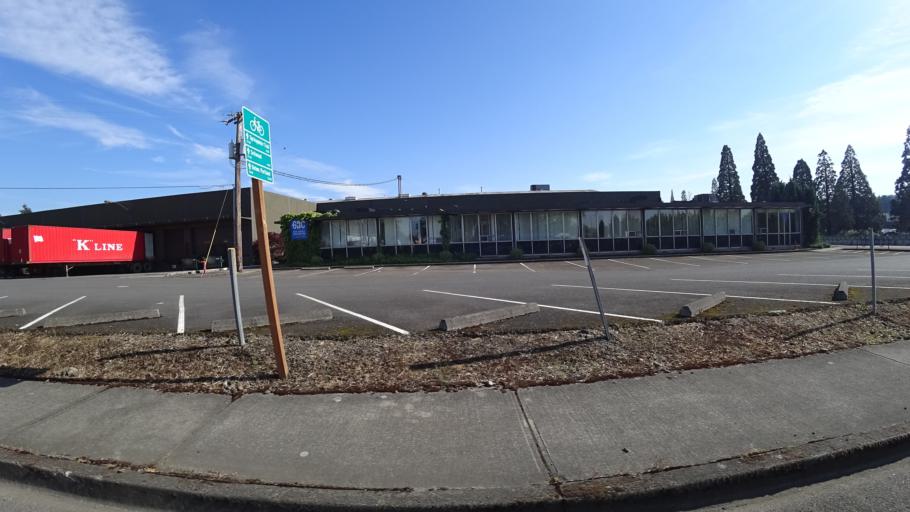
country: US
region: Oregon
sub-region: Clackamas County
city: Milwaukie
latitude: 45.4570
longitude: -122.6392
